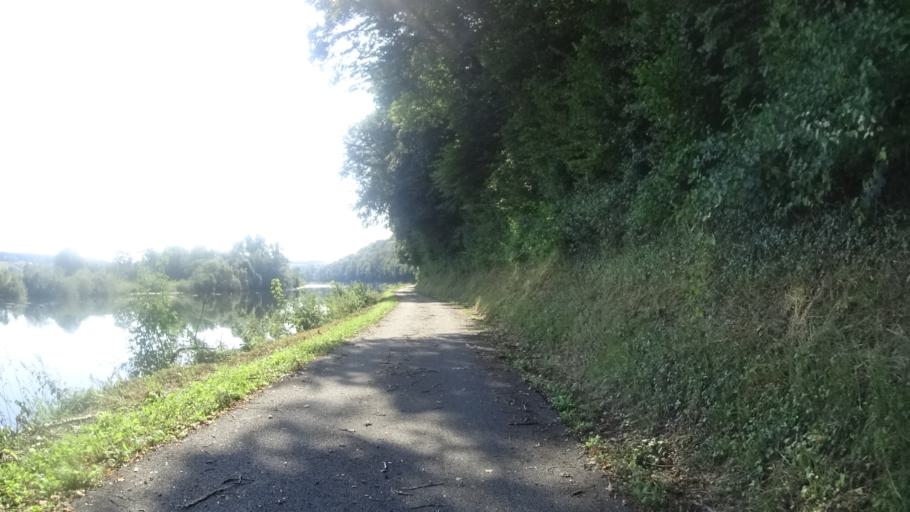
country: FR
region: Franche-Comte
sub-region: Departement du Doubs
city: Clerval
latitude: 47.4312
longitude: 6.5355
